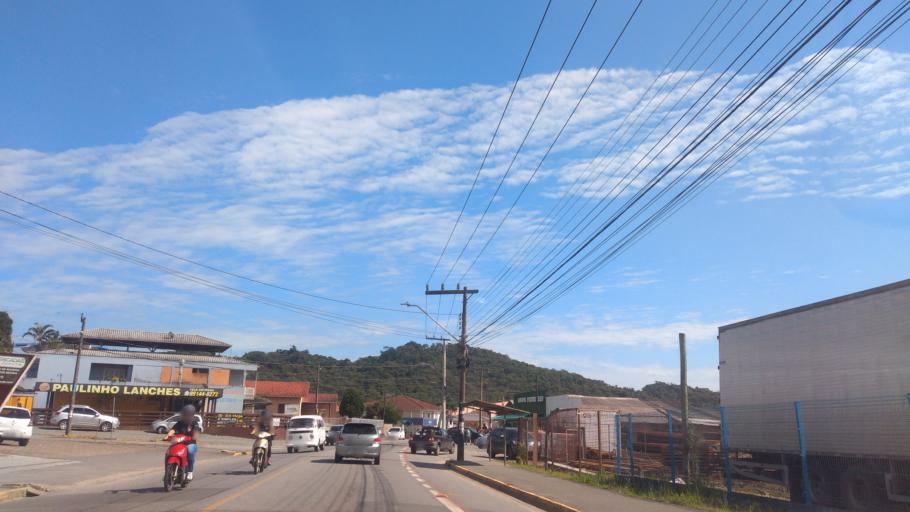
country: BR
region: Santa Catarina
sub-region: Joinville
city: Joinville
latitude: -26.2494
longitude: -48.8211
